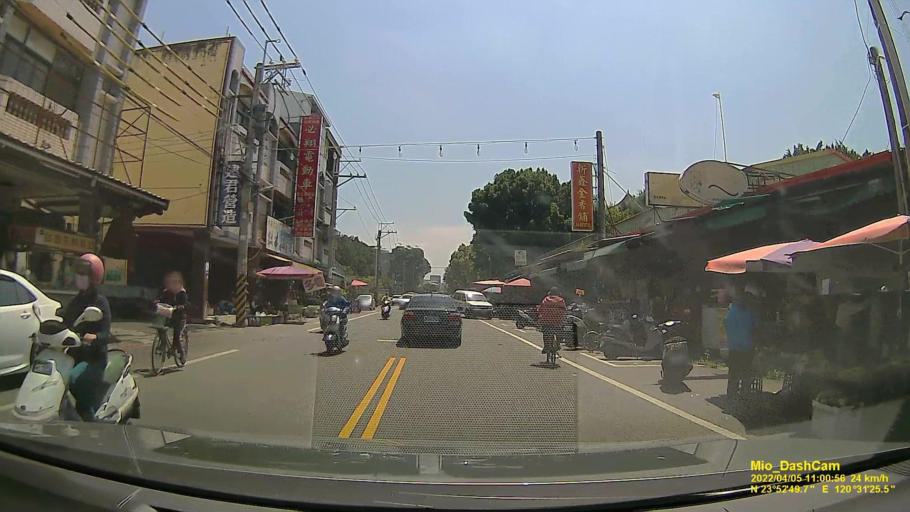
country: TW
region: Taiwan
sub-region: Nantou
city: Nantou
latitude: 23.8804
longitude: 120.5238
